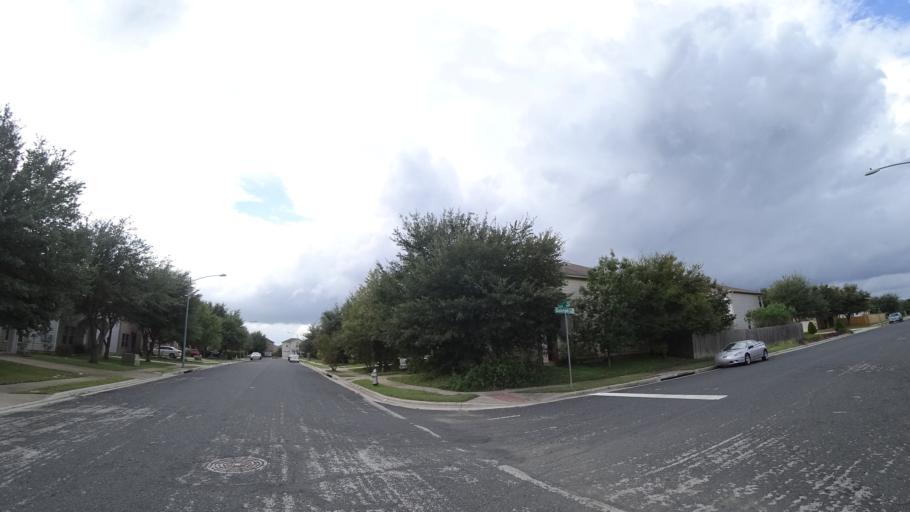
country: US
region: Texas
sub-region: Travis County
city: Onion Creek
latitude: 30.1509
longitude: -97.7379
